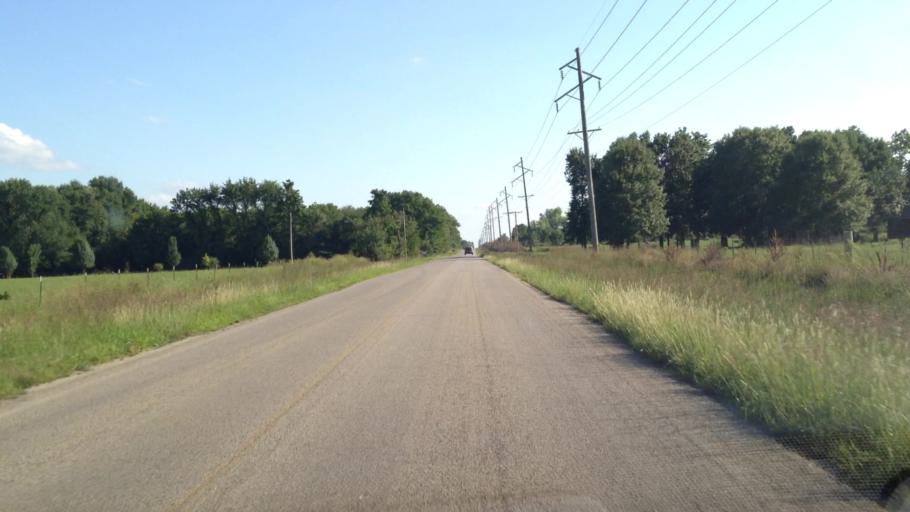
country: US
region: Kansas
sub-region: Crawford County
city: Frontenac
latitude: 37.4674
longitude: -94.6308
